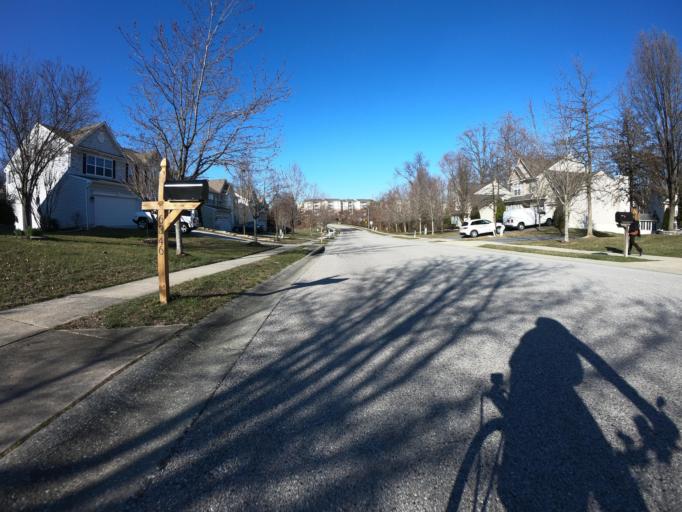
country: US
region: Maryland
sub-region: Howard County
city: West Elkridge
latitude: 39.2037
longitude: -76.7358
